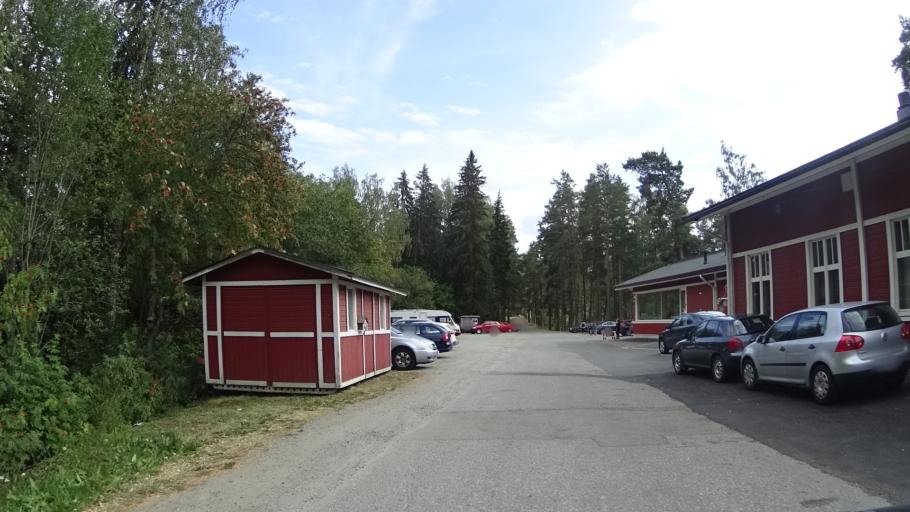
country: FI
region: Pirkanmaa
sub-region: Tampere
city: Kangasala
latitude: 61.4086
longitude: 24.1578
